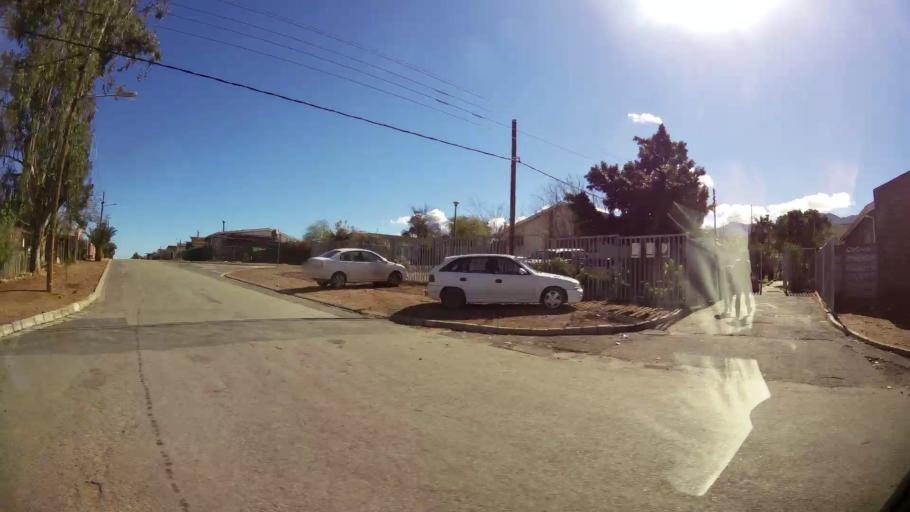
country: ZA
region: Western Cape
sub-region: Cape Winelands District Municipality
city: Ashton
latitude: -33.8334
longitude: 20.0461
